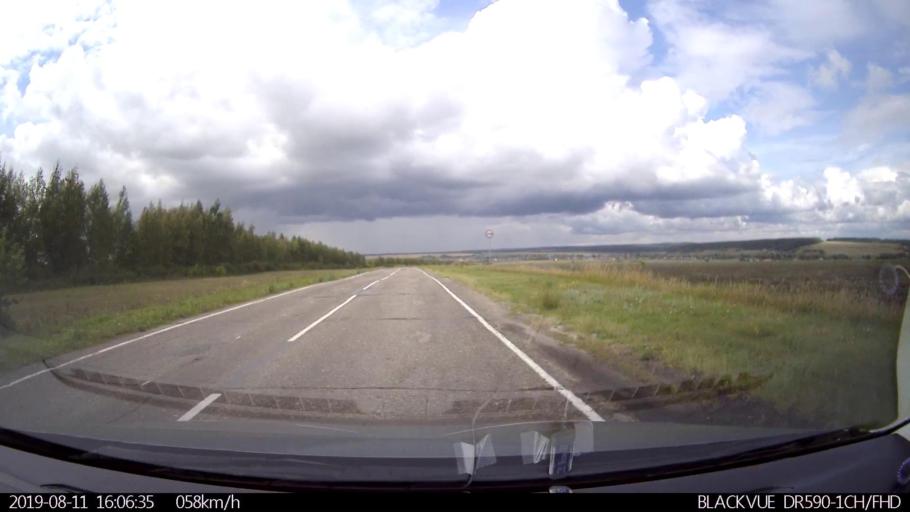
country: RU
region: Ulyanovsk
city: Ignatovka
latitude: 53.9703
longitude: 47.6480
